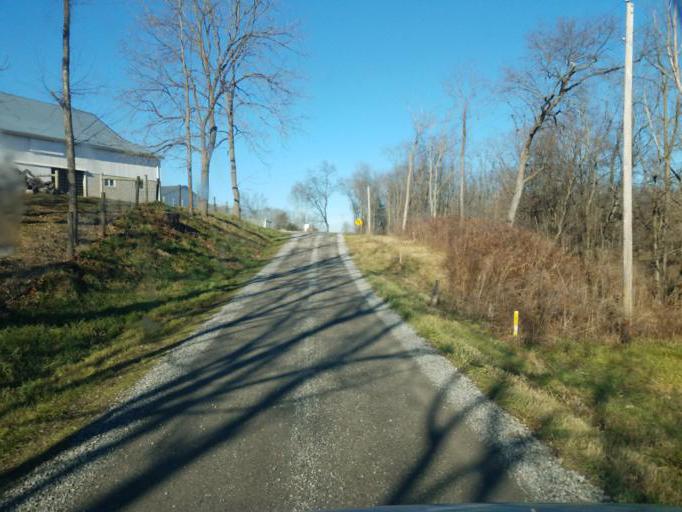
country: US
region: Ohio
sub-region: Wayne County
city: Apple Creek
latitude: 40.6664
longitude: -81.8278
